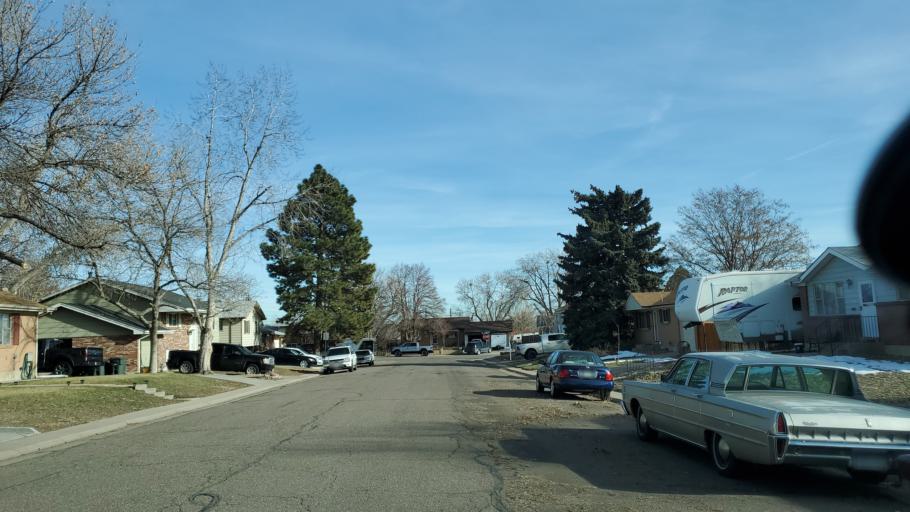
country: US
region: Colorado
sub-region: Adams County
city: Northglenn
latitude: 39.9056
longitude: -104.9617
